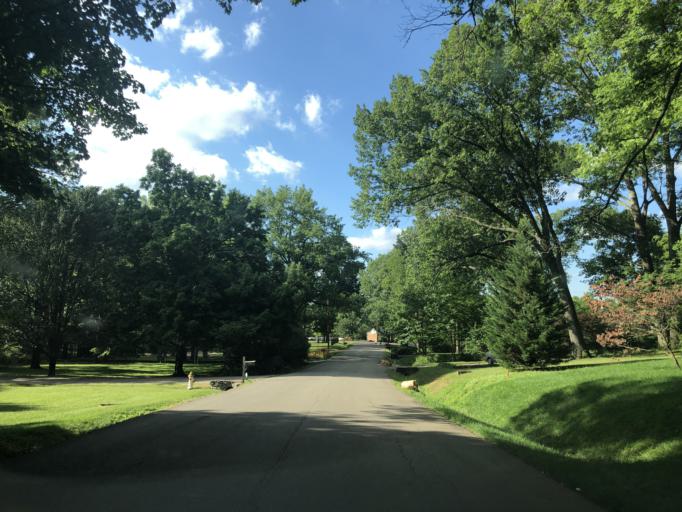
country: US
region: Tennessee
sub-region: Davidson County
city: Oak Hill
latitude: 36.0940
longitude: -86.8094
